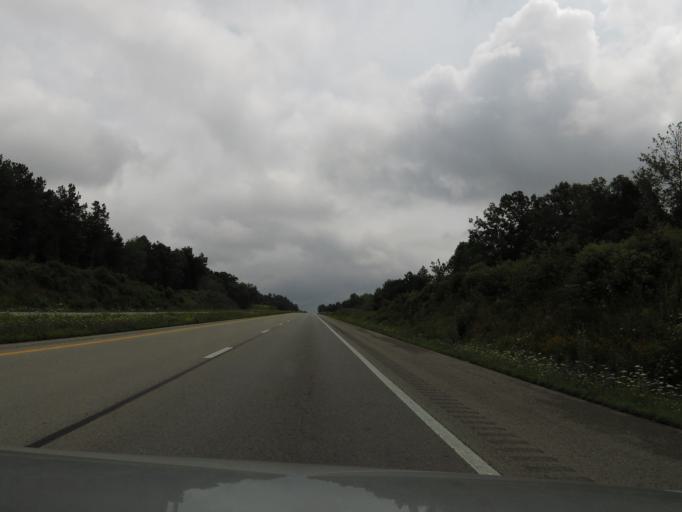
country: US
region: Kentucky
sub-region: Ohio County
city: Oak Grove
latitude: 37.3895
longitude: -86.6267
